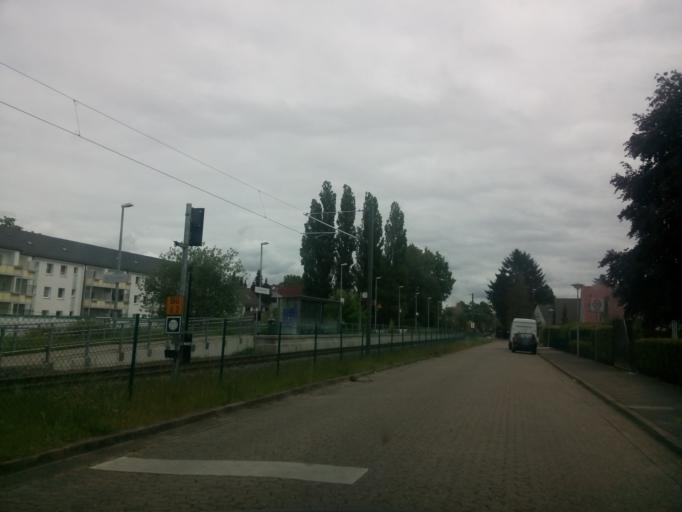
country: DE
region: Lower Saxony
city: Neuenkirchen
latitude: 53.1888
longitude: 8.5570
